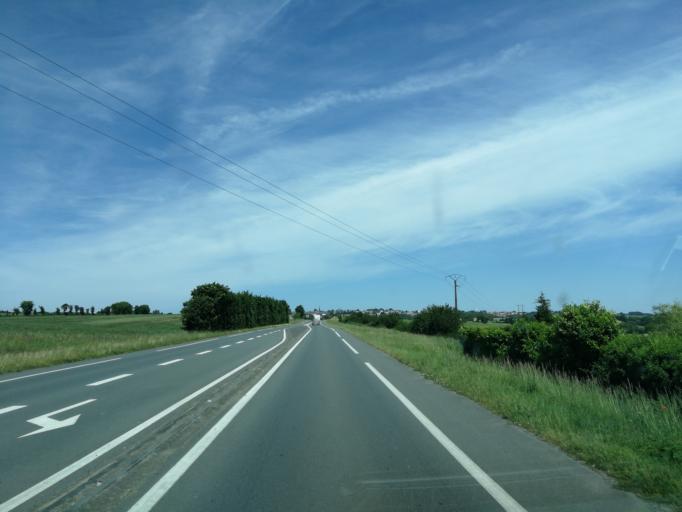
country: FR
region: Pays de la Loire
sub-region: Departement de la Vendee
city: Antigny
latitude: 46.6293
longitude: -0.7678
